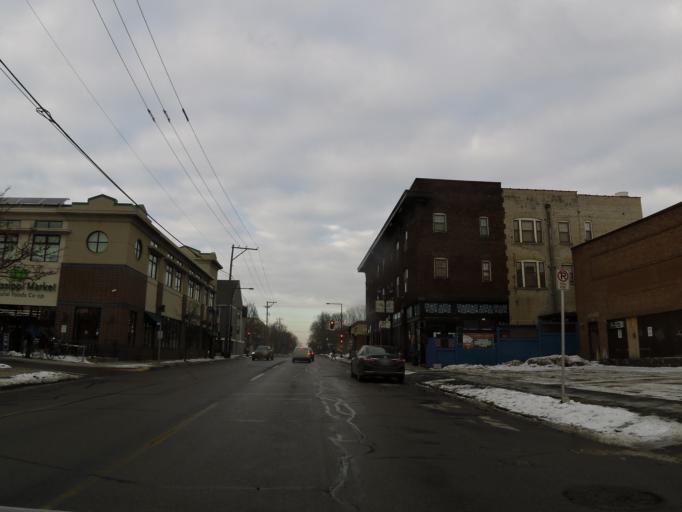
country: US
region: Minnesota
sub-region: Ramsey County
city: Saint Paul
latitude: 44.9459
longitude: -93.1263
